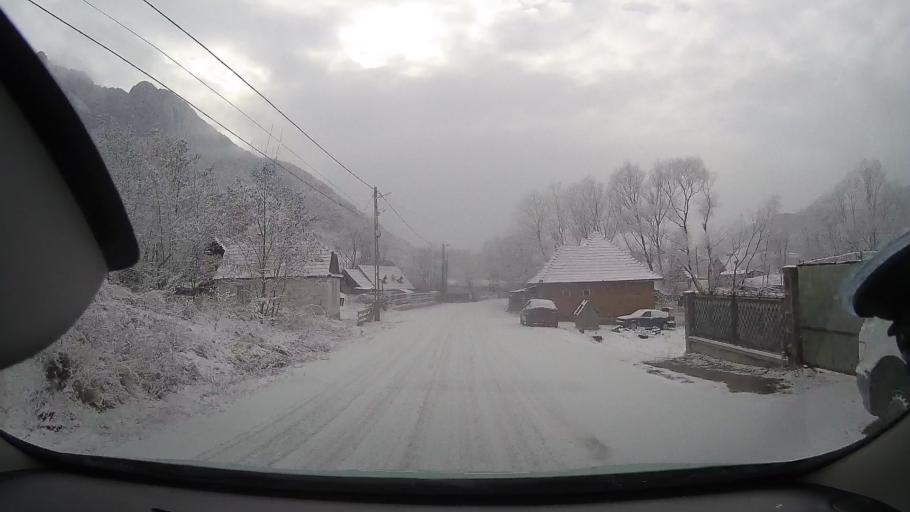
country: RO
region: Alba
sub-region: Comuna Rimetea
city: Rimetea
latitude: 46.4594
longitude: 23.5715
